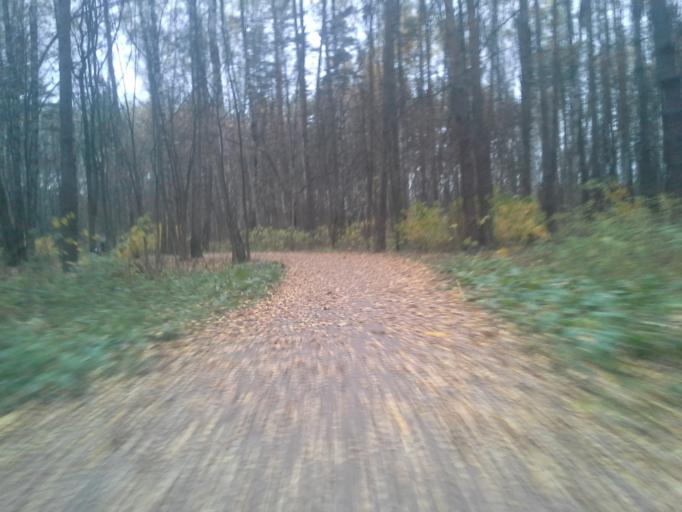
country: RU
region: Moskovskaya
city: Zarech'ye
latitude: 55.6672
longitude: 37.3885
